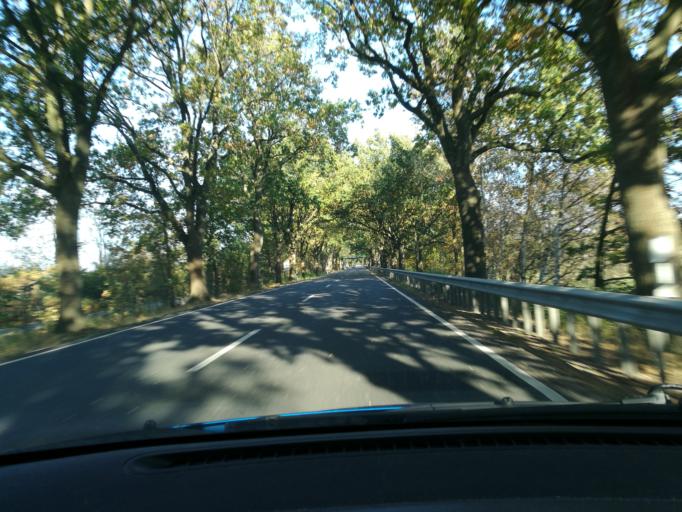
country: DE
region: Lower Saxony
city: Klein Gusborn
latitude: 53.1087
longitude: 11.1870
